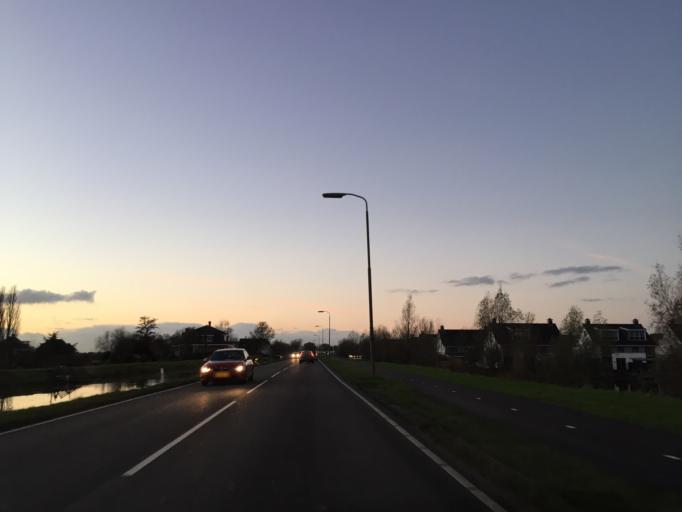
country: NL
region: South Holland
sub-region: Gemeente Lansingerland
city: Berkel en Rodenrijs
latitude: 51.9936
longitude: 4.4628
